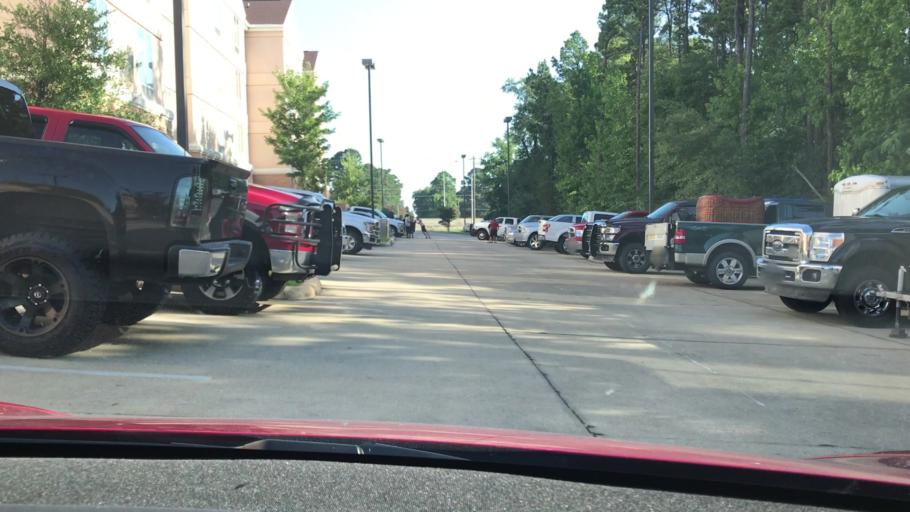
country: US
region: Louisiana
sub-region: Caddo Parish
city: Greenwood
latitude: 32.4508
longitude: -93.8564
